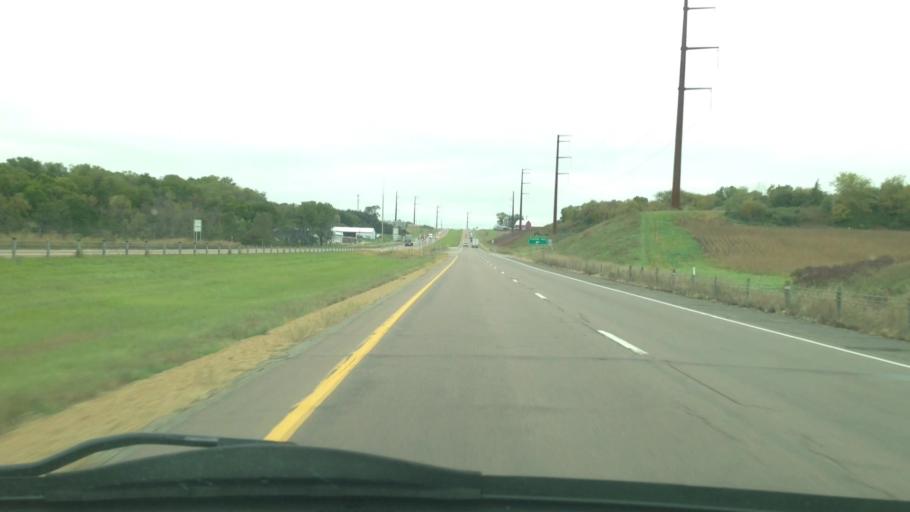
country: US
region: Minnesota
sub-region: Goodhue County
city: Cannon Falls
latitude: 44.5770
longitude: -92.9689
